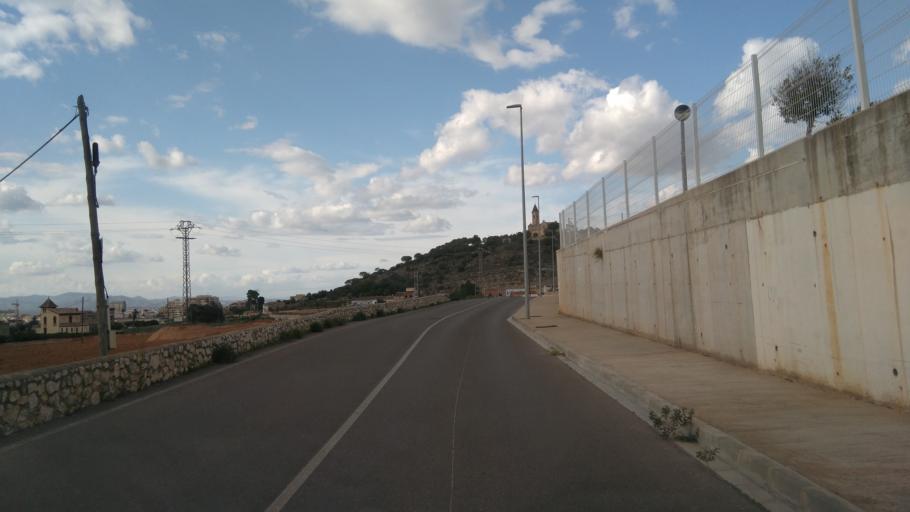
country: ES
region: Valencia
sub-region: Provincia de Valencia
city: Alzira
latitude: 39.1474
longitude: -0.4154
